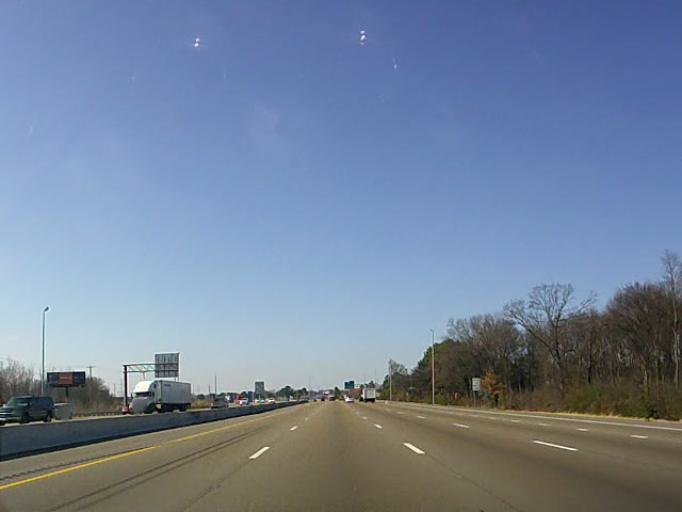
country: US
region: Tennessee
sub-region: Shelby County
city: New South Memphis
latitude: 35.0824
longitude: -89.9481
